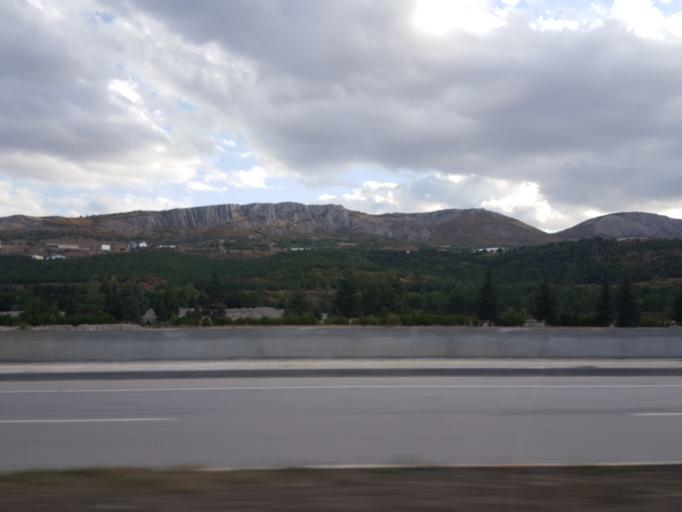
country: TR
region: Tokat
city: Tokat
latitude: 40.3353
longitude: 36.5077
